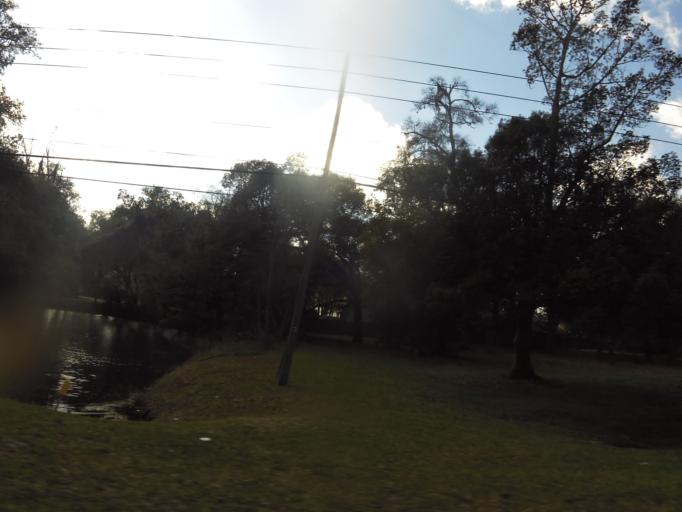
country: US
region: Florida
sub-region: Volusia County
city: North DeLand
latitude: 29.0843
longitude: -81.3204
